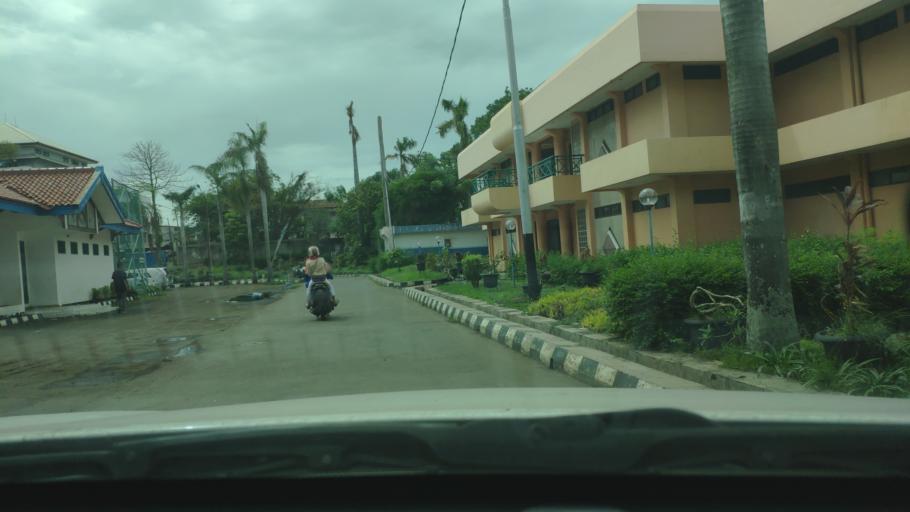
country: ID
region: West Java
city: Ciputat
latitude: -6.2234
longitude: 106.7071
